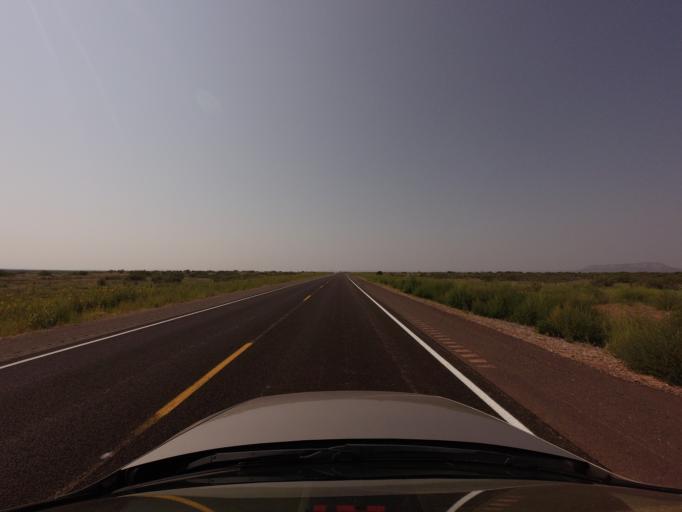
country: US
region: New Mexico
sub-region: Quay County
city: Tucumcari
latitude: 34.9757
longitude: -103.7516
